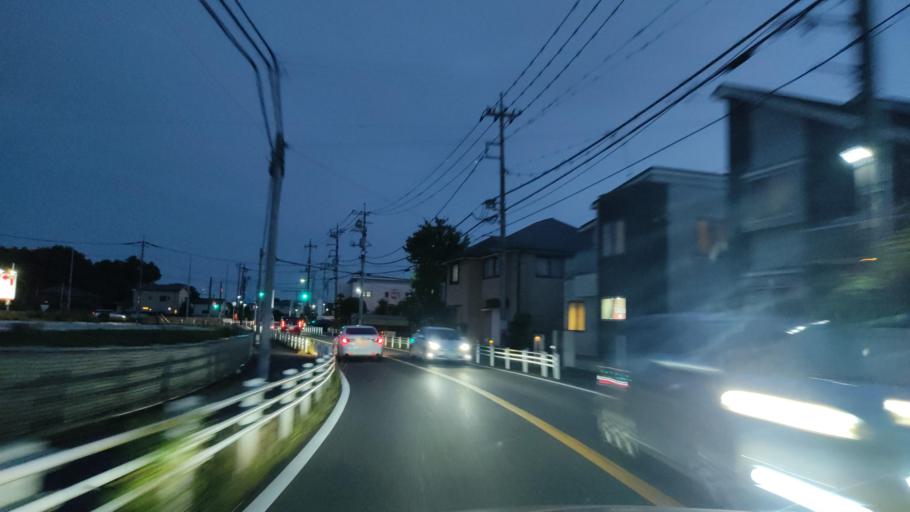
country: JP
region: Chiba
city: Nagareyama
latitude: 35.8522
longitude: 139.9111
